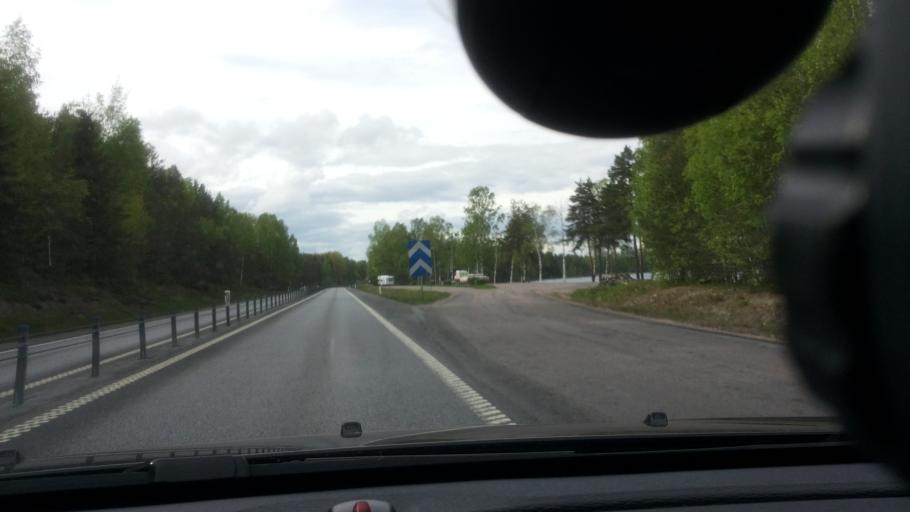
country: SE
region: Gaevleborg
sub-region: Gavle Kommun
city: Norrsundet
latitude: 61.0031
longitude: 16.9888
